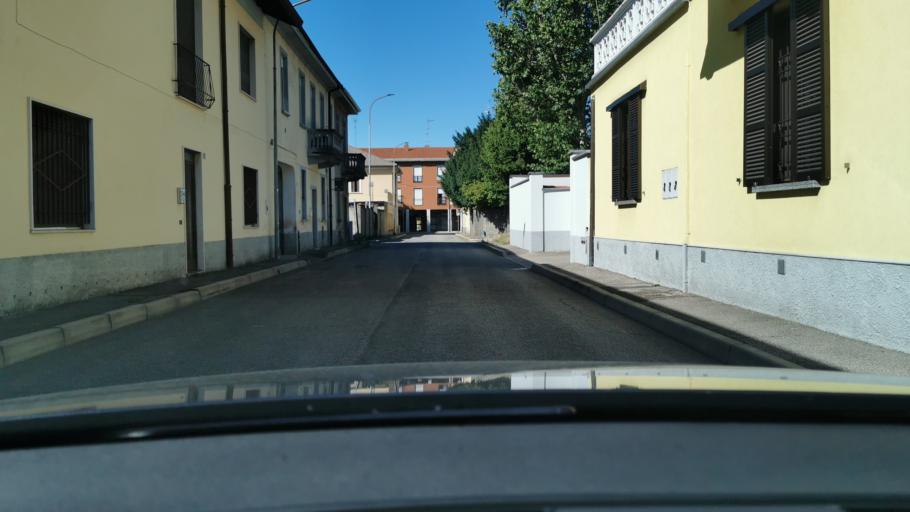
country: IT
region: Lombardy
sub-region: Citta metropolitana di Milano
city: Rescaldina
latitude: 45.6205
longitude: 8.9466
